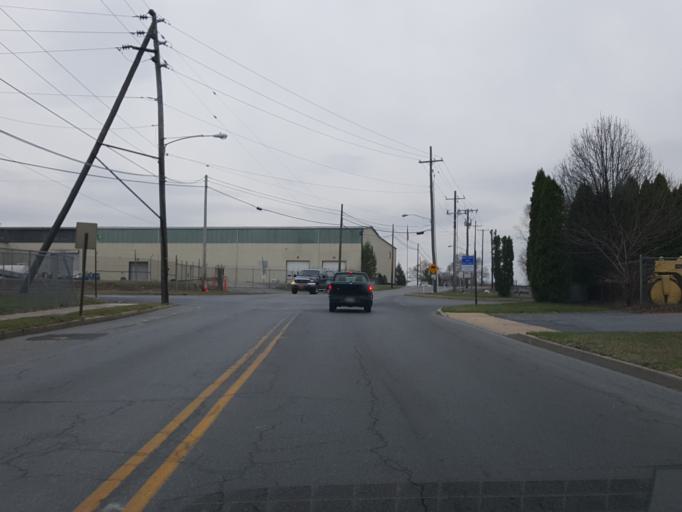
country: US
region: Pennsylvania
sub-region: Lebanon County
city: Pleasant Hill
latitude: 40.3445
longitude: -76.4409
